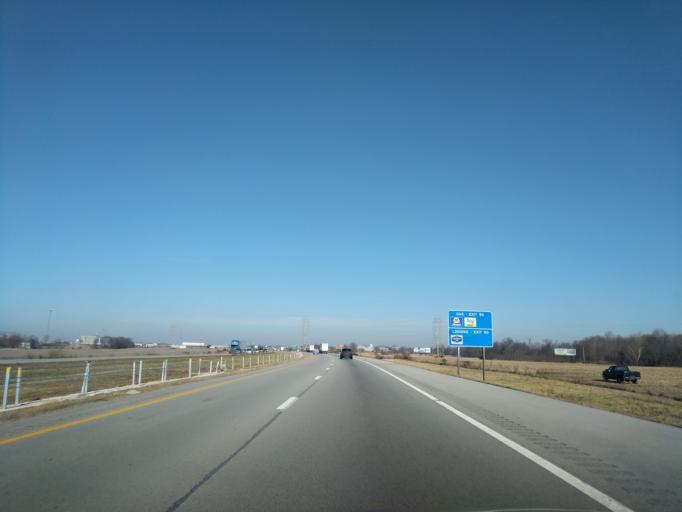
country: US
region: Ohio
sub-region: Shelby County
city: Sidney
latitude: 40.2523
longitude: -84.1836
